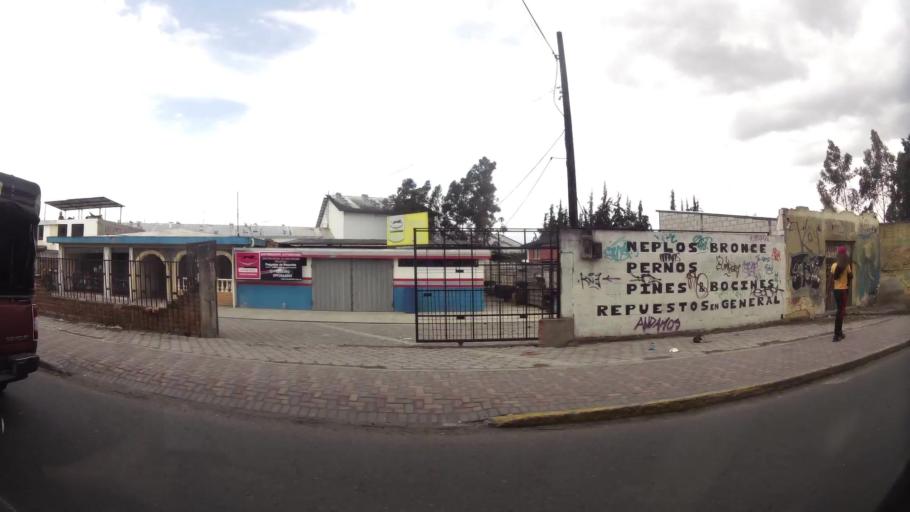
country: EC
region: Pichincha
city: Quito
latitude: -0.0883
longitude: -78.4263
